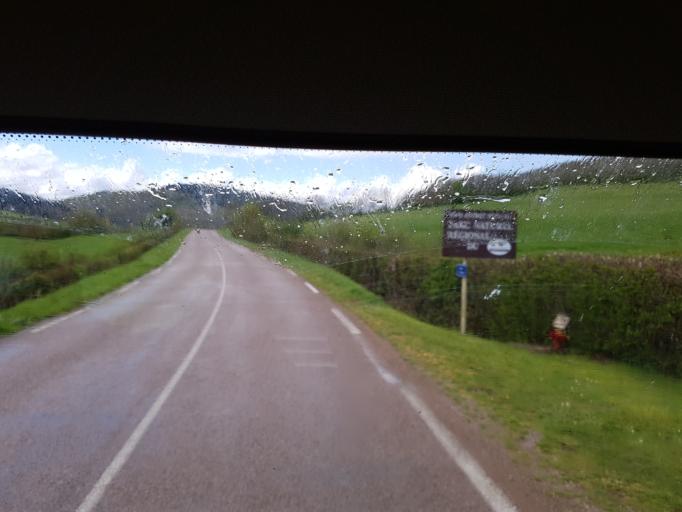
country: FR
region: Bourgogne
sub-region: Departement de Saone-et-Loire
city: Autun
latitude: 47.0600
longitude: 4.2612
